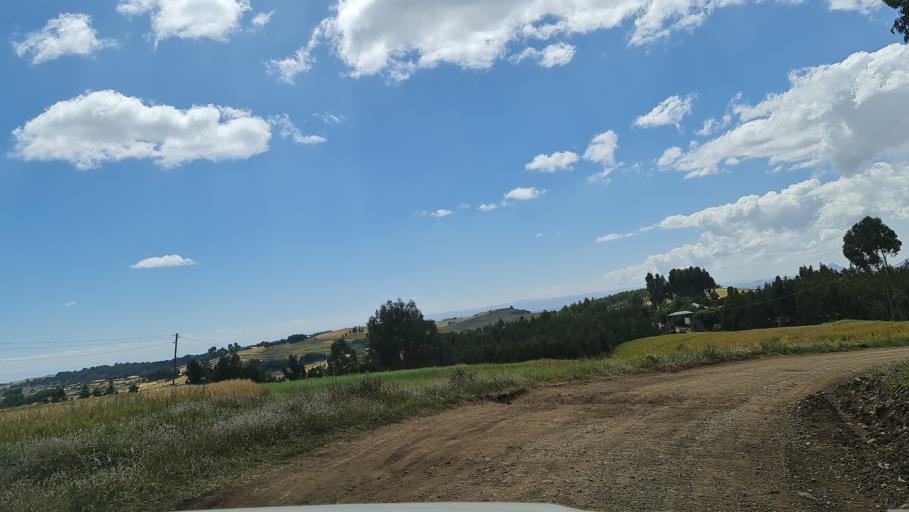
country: ET
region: Amhara
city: Debark'
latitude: 13.1675
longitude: 37.9642
